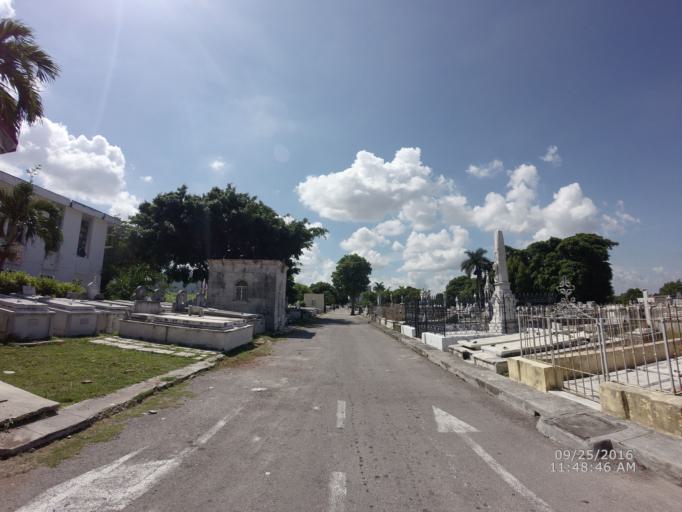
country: CU
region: La Habana
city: Havana
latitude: 23.1256
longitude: -82.3947
